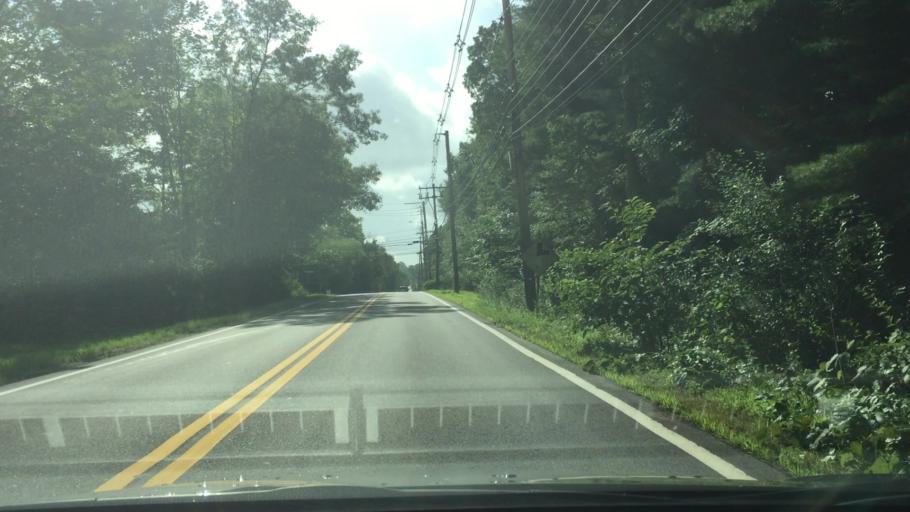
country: US
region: Massachusetts
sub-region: Middlesex County
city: Stow
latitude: 42.4796
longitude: -71.4963
